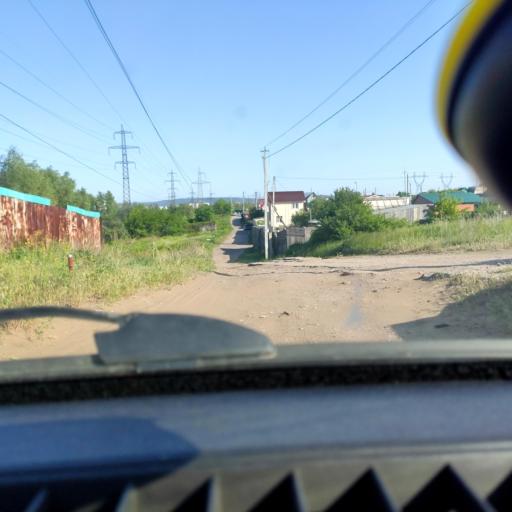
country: RU
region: Samara
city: Zhigulevsk
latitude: 53.4951
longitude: 49.4974
